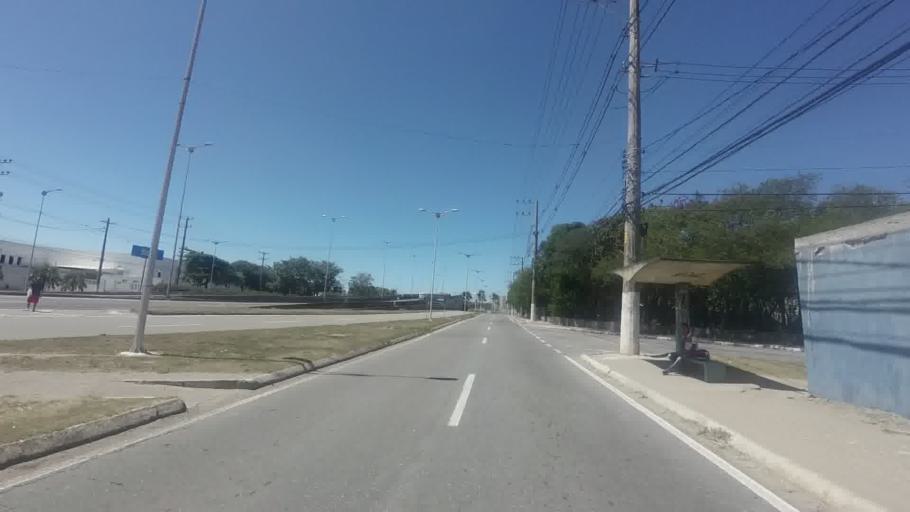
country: BR
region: Espirito Santo
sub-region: Vila Velha
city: Vila Velha
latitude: -20.2321
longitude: -40.2779
